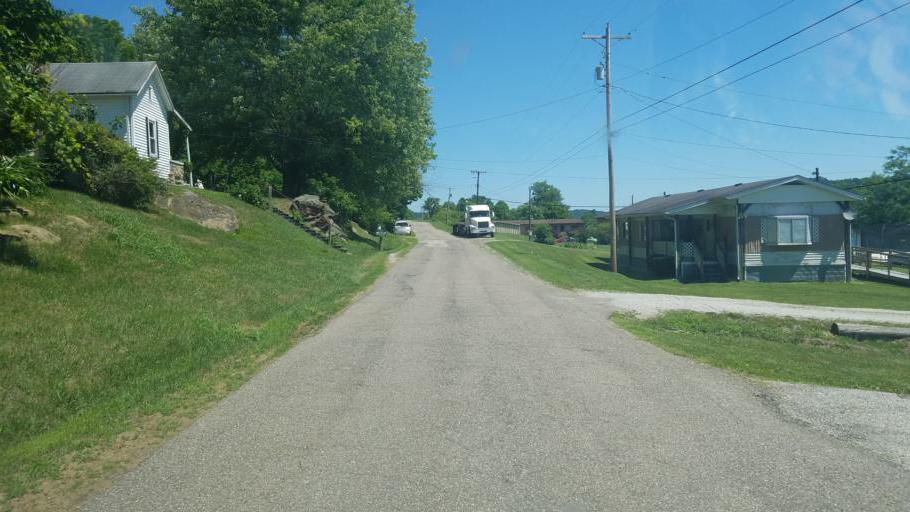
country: US
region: West Virginia
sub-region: Cabell County
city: Lesage
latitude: 38.5538
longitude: -82.2953
